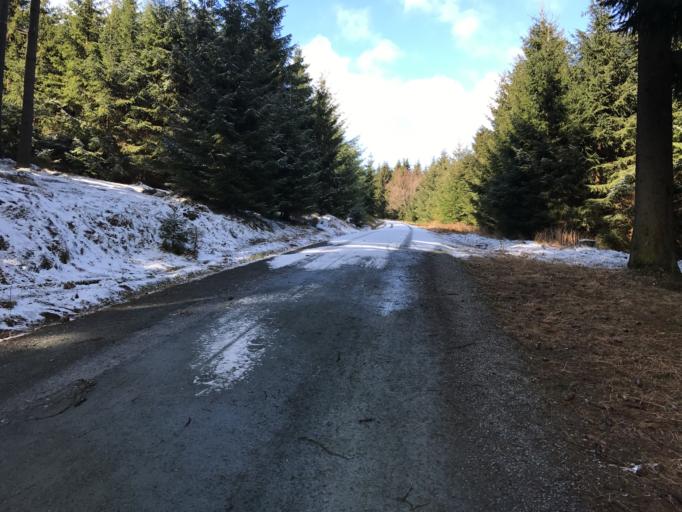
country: DE
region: Hesse
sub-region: Regierungsbezirk Darmstadt
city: Konigstein im Taunus
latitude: 50.2204
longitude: 8.4608
